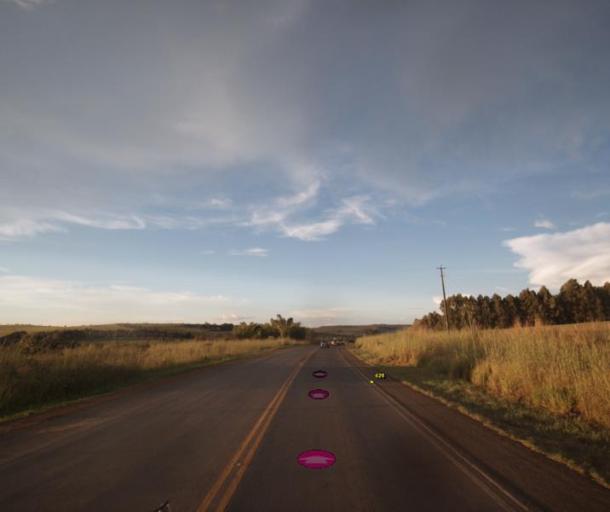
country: BR
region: Goias
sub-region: Anapolis
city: Anapolis
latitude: -16.1731
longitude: -48.9007
